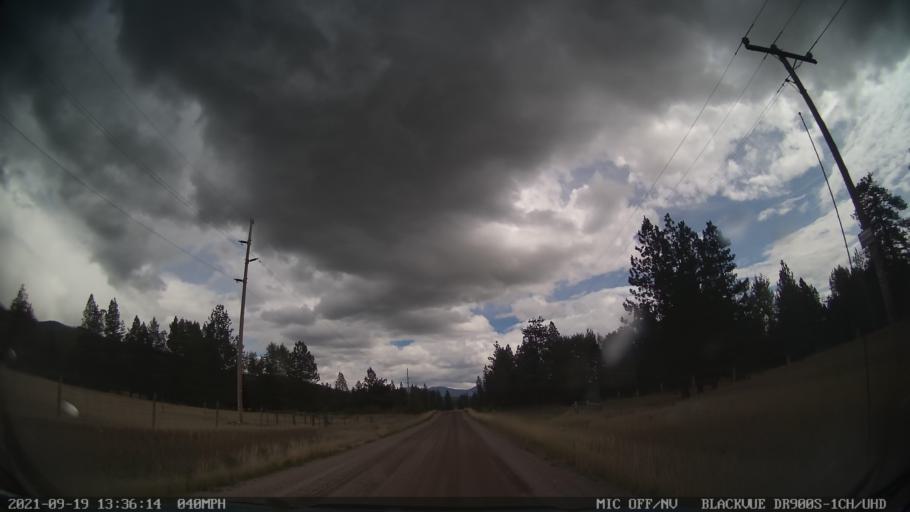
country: US
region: Montana
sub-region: Missoula County
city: Seeley Lake
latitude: 47.1065
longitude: -113.3006
